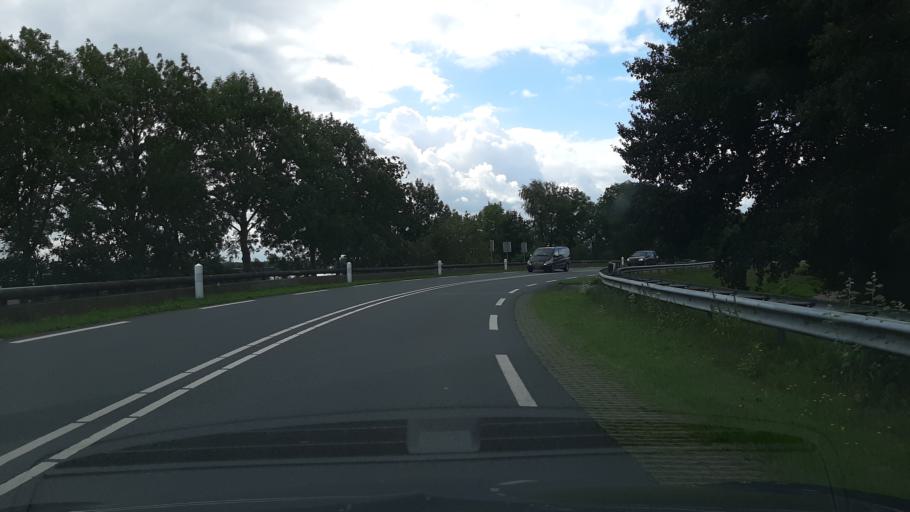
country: NL
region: Overijssel
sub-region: Gemeente Steenwijkerland
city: Wanneperveen
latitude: 52.6933
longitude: 6.0778
